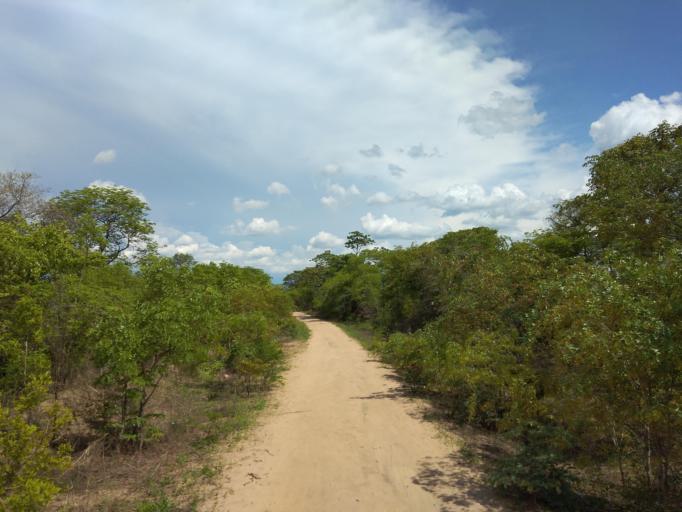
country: ZM
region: Eastern
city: Nyimba
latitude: -14.1145
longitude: 30.1251
